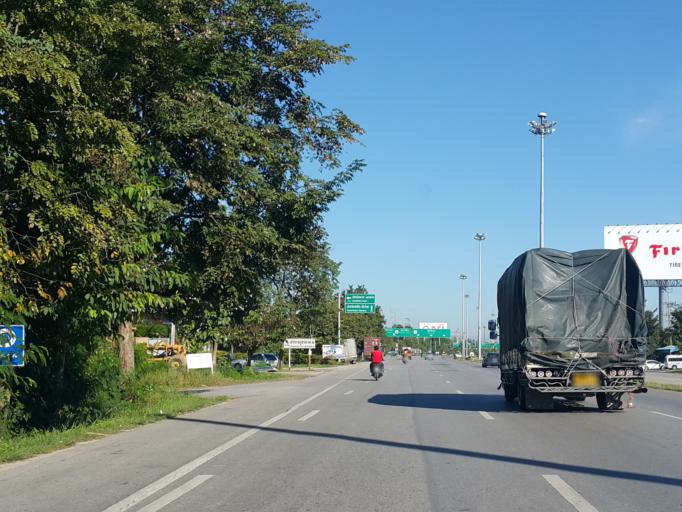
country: TH
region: Chiang Mai
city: Saraphi
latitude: 18.7561
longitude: 99.0310
